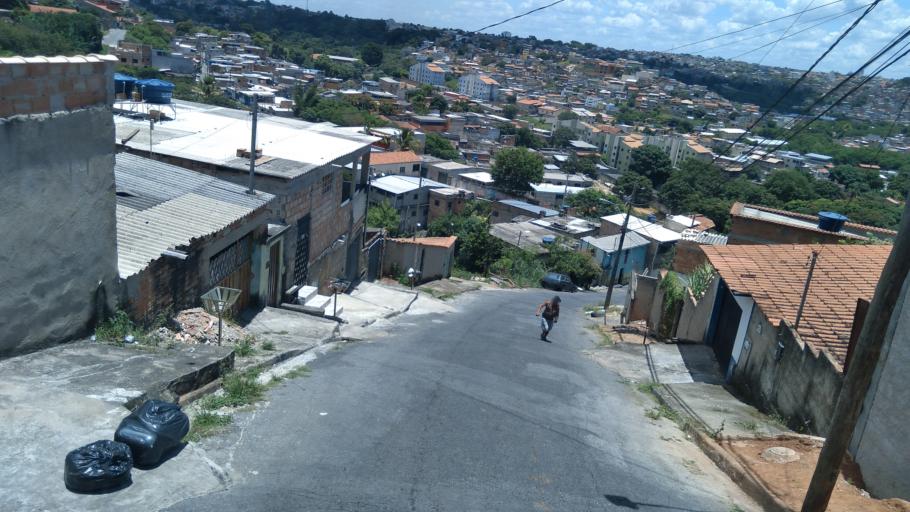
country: BR
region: Minas Gerais
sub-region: Santa Luzia
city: Santa Luzia
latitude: -19.8422
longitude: -43.8966
